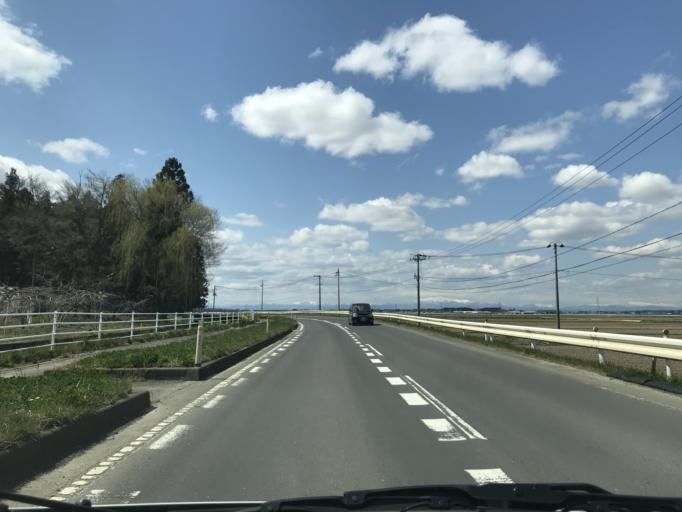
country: JP
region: Miyagi
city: Wakuya
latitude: 38.6466
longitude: 141.2523
